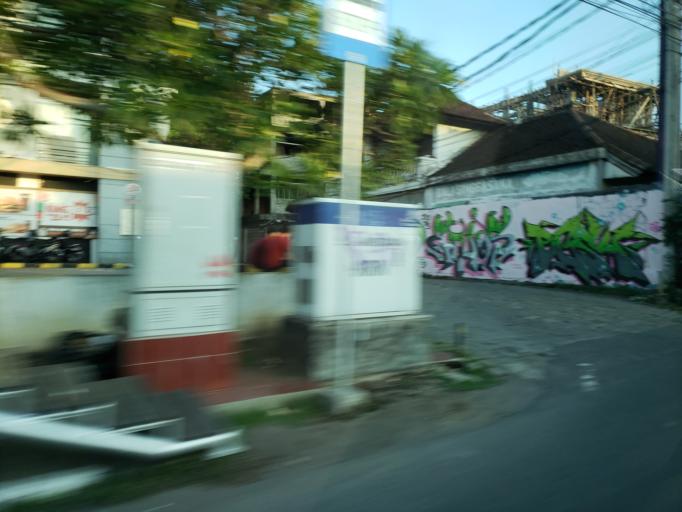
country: ID
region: Bali
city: Kelanabian
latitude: -8.7616
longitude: 115.1790
